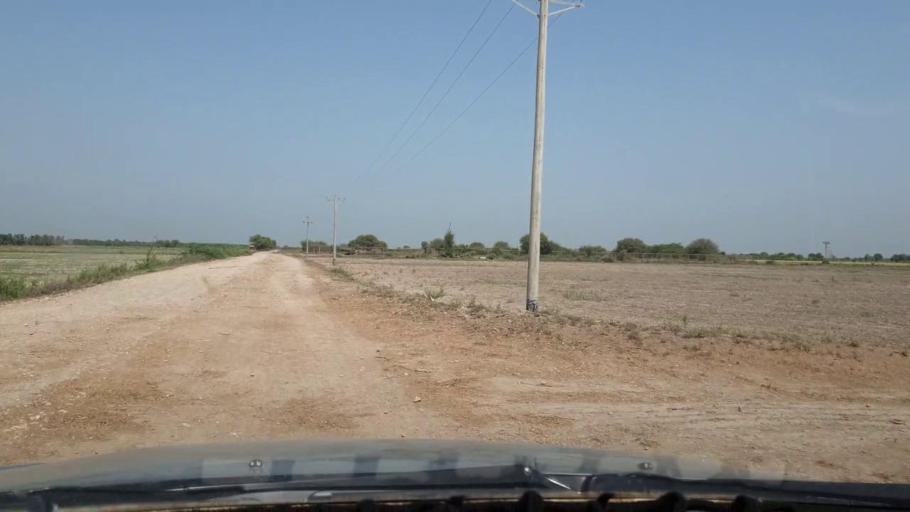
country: PK
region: Sindh
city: Tando Muhammad Khan
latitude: 25.1562
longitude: 68.6338
